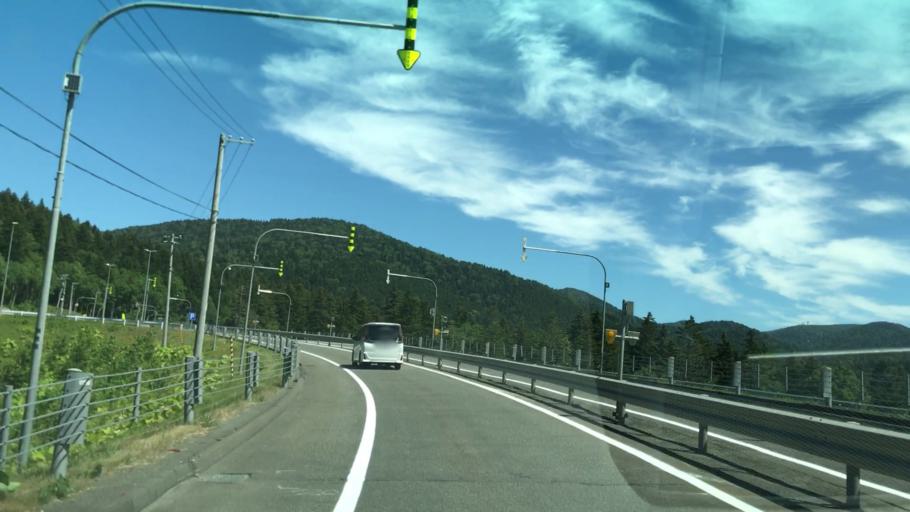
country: JP
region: Hokkaido
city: Shimo-furano
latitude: 42.9664
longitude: 142.6734
